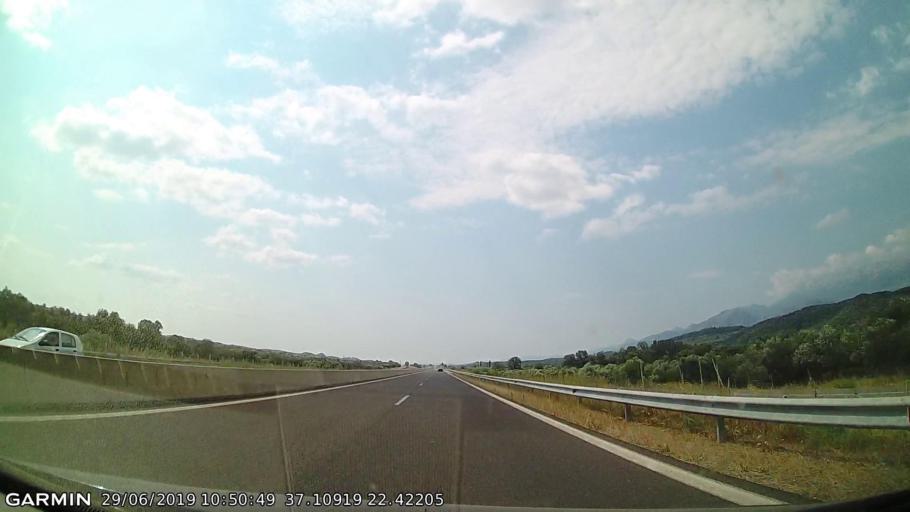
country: GR
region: Peloponnese
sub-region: Nomos Lakonias
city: Magoula
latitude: 37.1087
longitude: 22.4223
